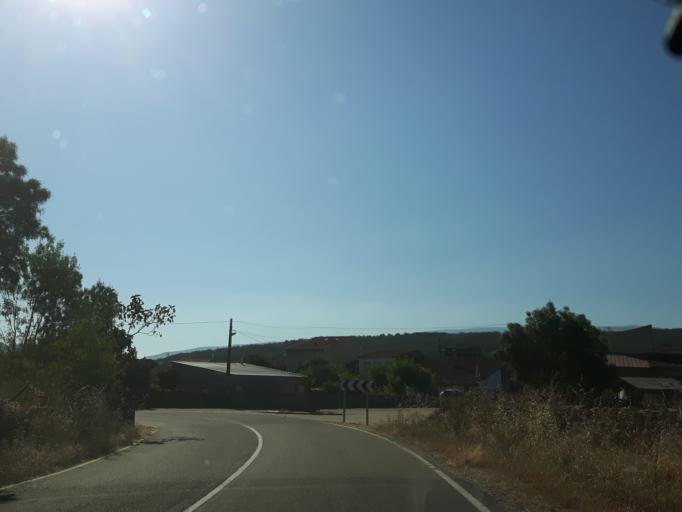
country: ES
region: Castille and Leon
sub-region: Provincia de Salamanca
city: Valdehijaderos
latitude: 40.4194
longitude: -5.8503
